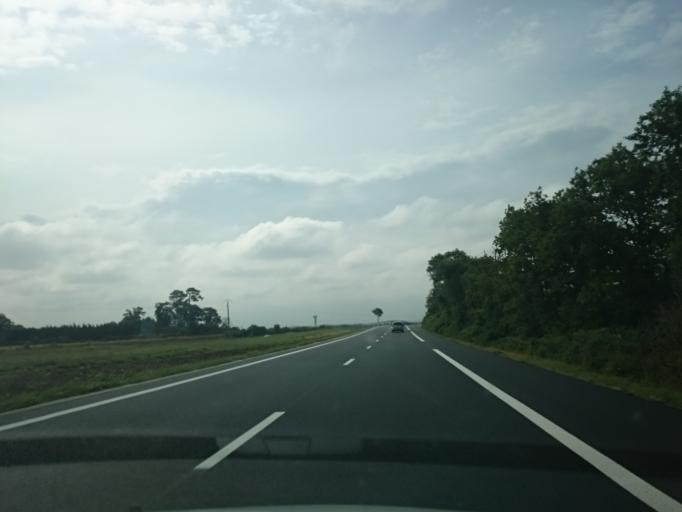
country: FR
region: Brittany
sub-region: Departement du Morbihan
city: Ambon
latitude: 47.5712
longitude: -2.5184
